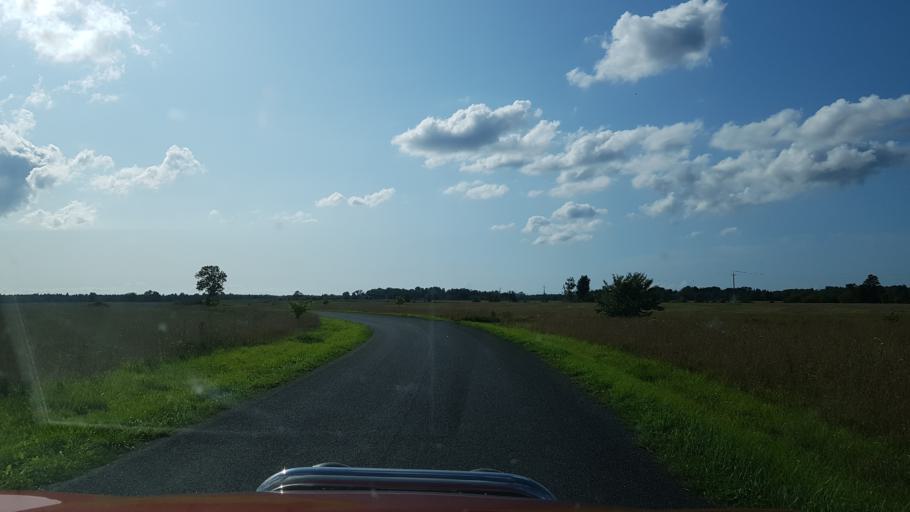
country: EE
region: Harju
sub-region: Paldiski linn
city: Paldiski
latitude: 59.1996
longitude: 23.9589
